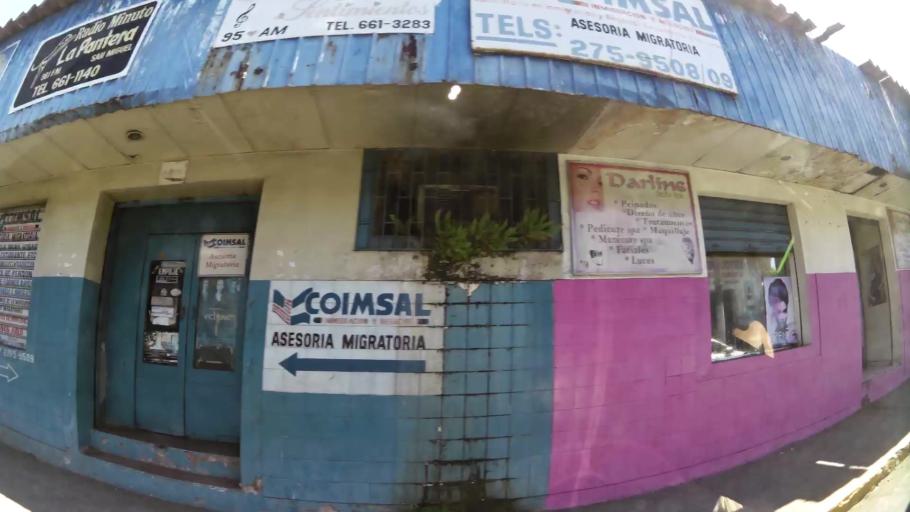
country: SV
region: San Miguel
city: San Miguel
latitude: 13.4794
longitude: -88.1742
